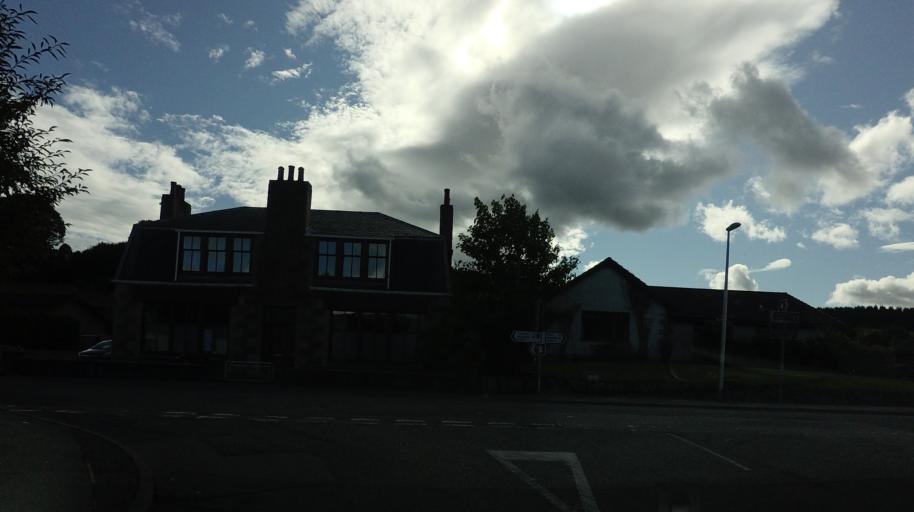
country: GB
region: Scotland
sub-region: Aberdeenshire
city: Torphins
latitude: 57.1265
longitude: -2.6882
